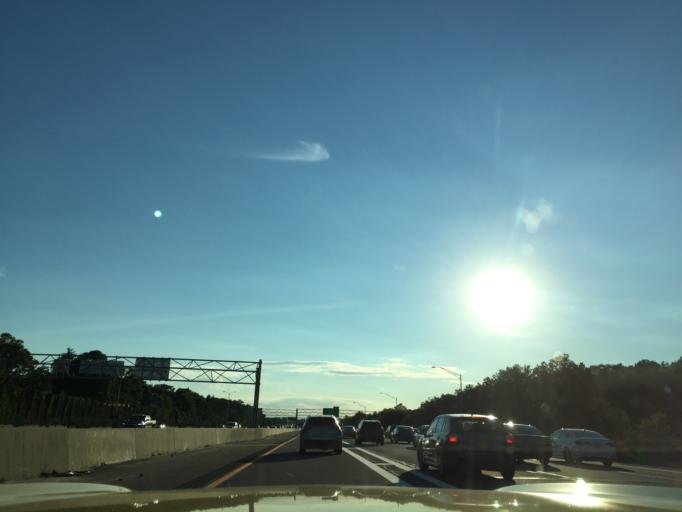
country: US
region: New York
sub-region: Suffolk County
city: Medford
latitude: 40.8241
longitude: -73.0038
